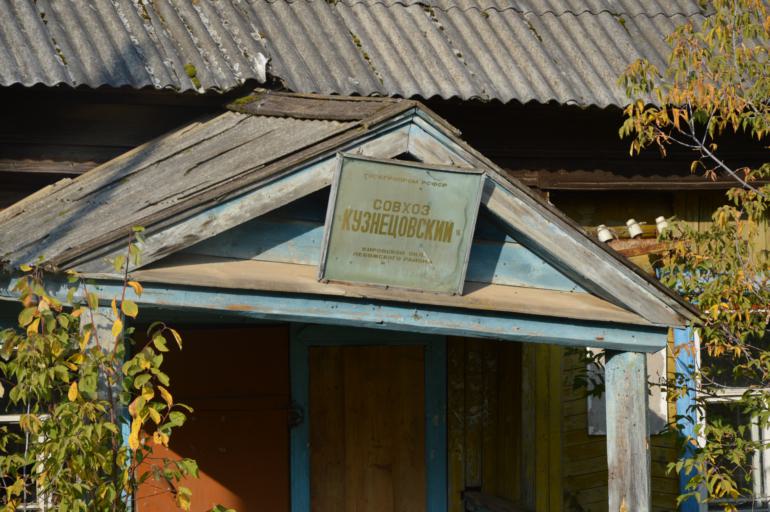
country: RU
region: Mariy-El
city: Sernur
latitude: 57.0476
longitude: 49.2579
